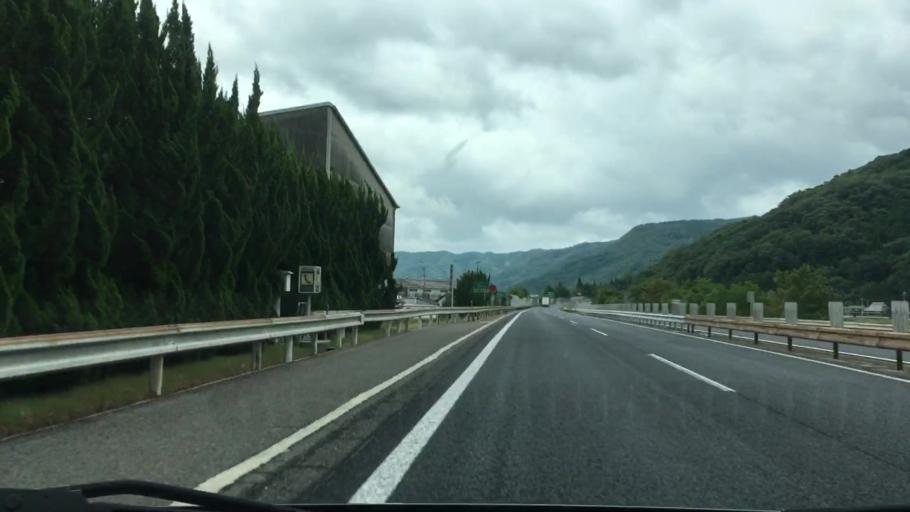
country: JP
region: Okayama
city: Niimi
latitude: 34.9712
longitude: 133.6508
